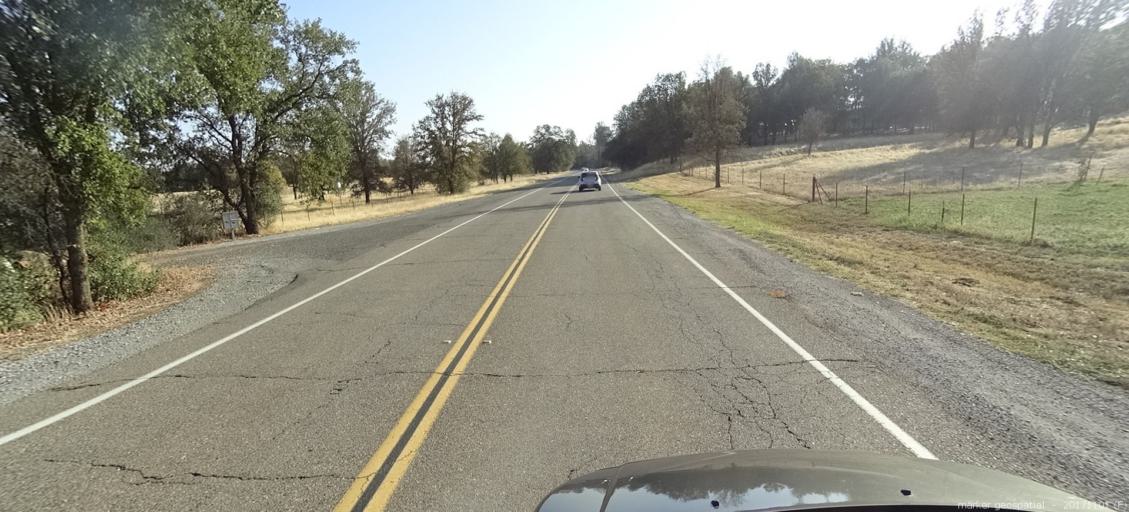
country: US
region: California
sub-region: Shasta County
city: Shasta Lake
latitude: 40.6355
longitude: -122.3259
